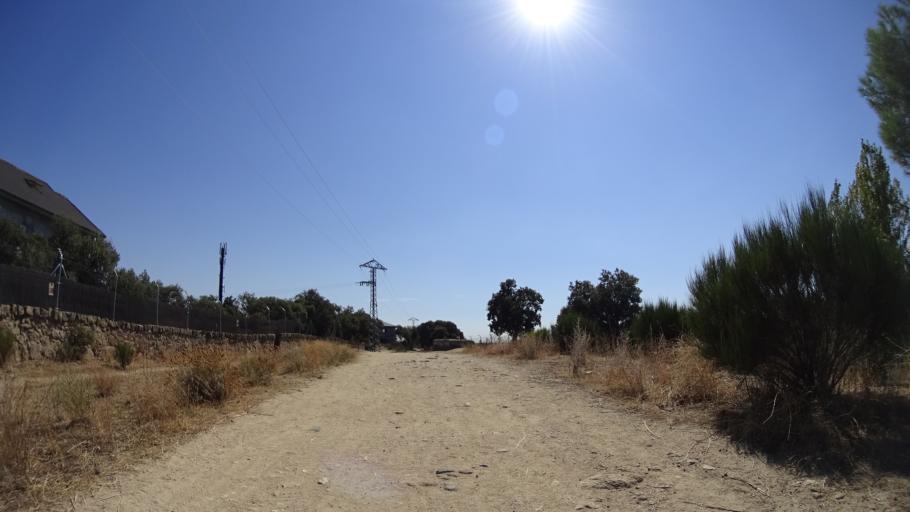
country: ES
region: Madrid
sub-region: Provincia de Madrid
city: Galapagar
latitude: 40.6054
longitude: -4.0113
